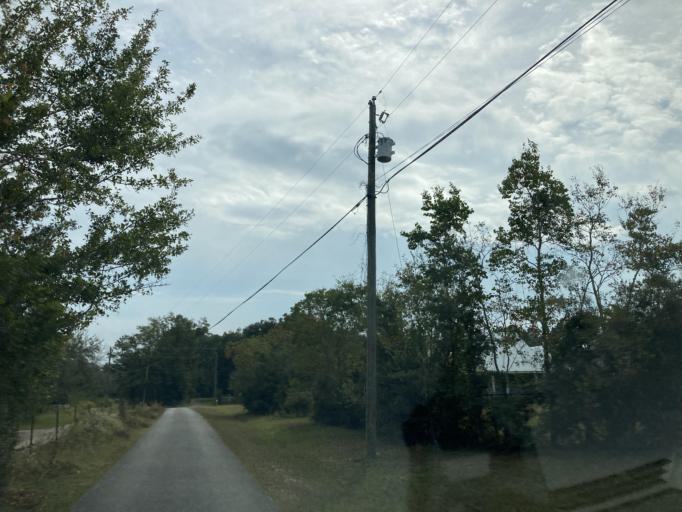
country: US
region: Mississippi
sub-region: Jackson County
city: Saint Martin
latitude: 30.4659
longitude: -88.8602
